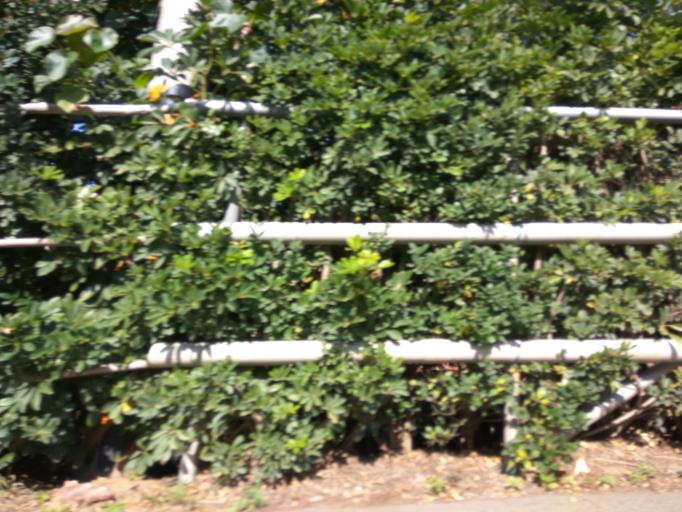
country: TW
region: Taiwan
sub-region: Hsinchu
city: Zhubei
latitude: 25.0353
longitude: 121.0540
